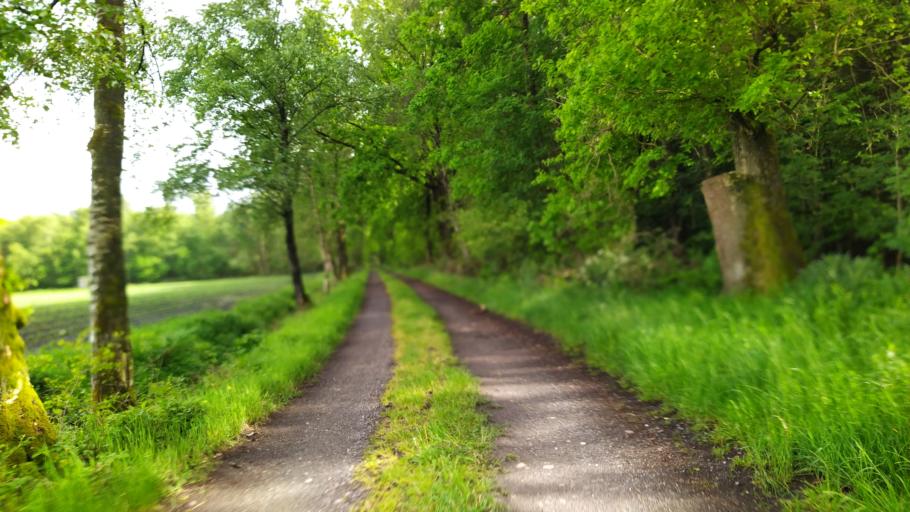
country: DE
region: Lower Saxony
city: Brest
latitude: 53.4255
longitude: 9.3558
